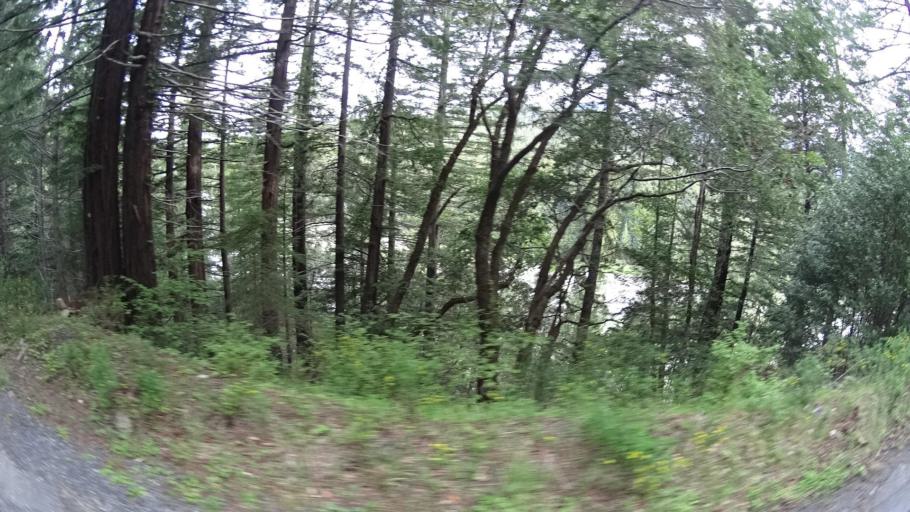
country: US
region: California
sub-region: Humboldt County
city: Redway
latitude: 40.3389
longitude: -123.8655
